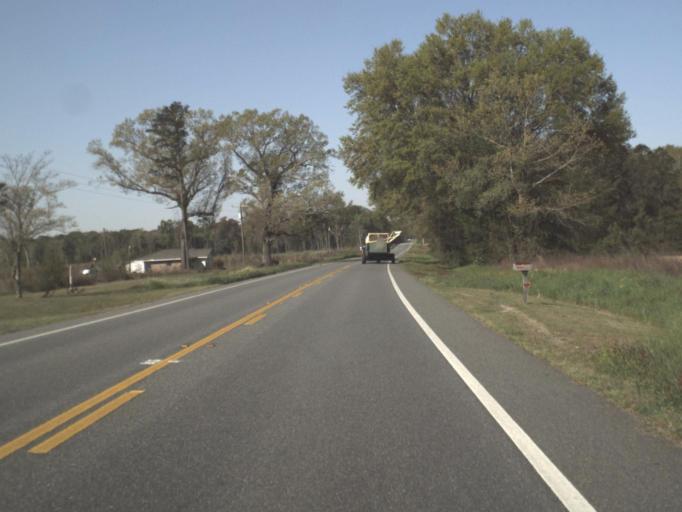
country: US
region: Florida
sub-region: Jackson County
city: Malone
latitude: 30.9488
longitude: -85.2512
